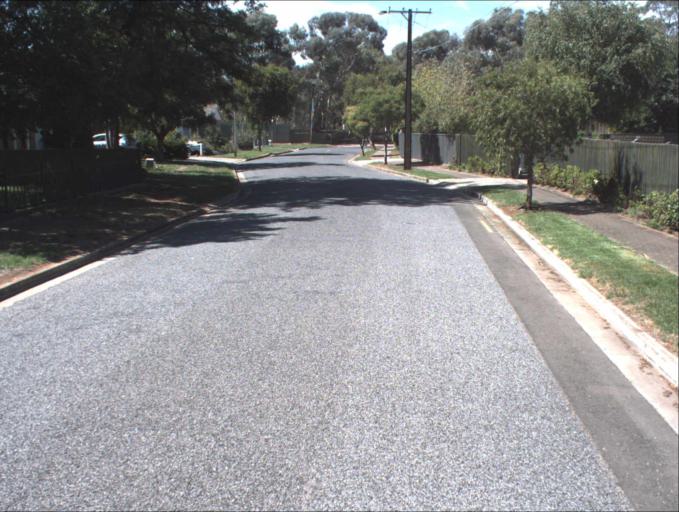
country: AU
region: South Australia
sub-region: Port Adelaide Enfield
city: Klemzig
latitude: -34.8832
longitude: 138.6431
